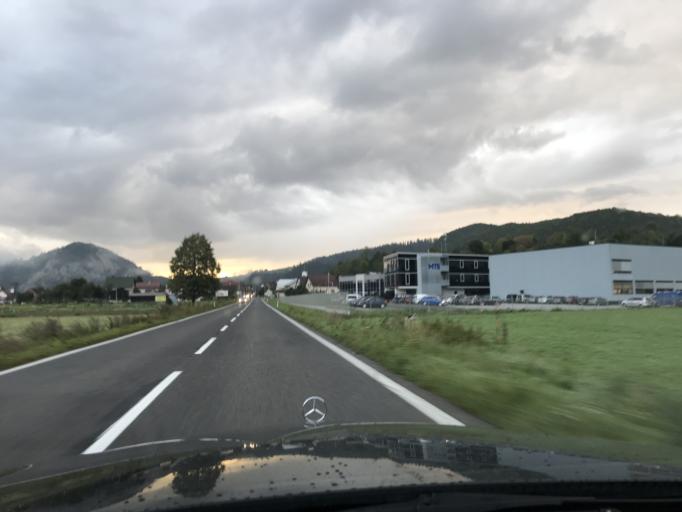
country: SK
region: Zilinsky
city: Tvrdosin
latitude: 49.2799
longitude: 19.4723
